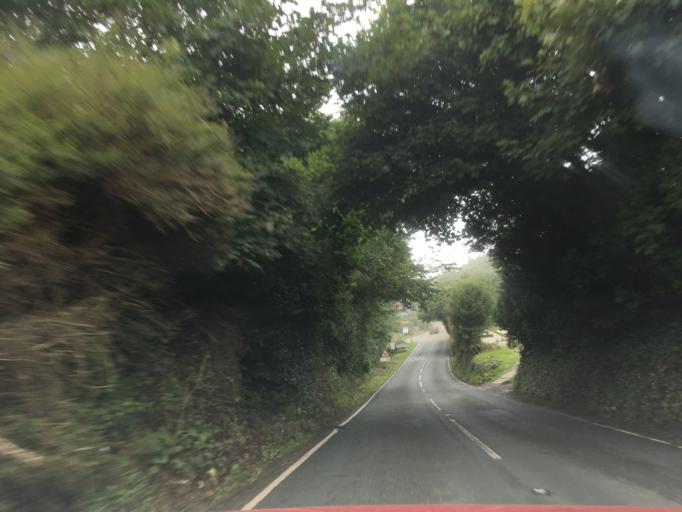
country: GB
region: Wales
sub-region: Pembrokeshire
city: Saint David's
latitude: 51.8784
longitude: -5.2148
